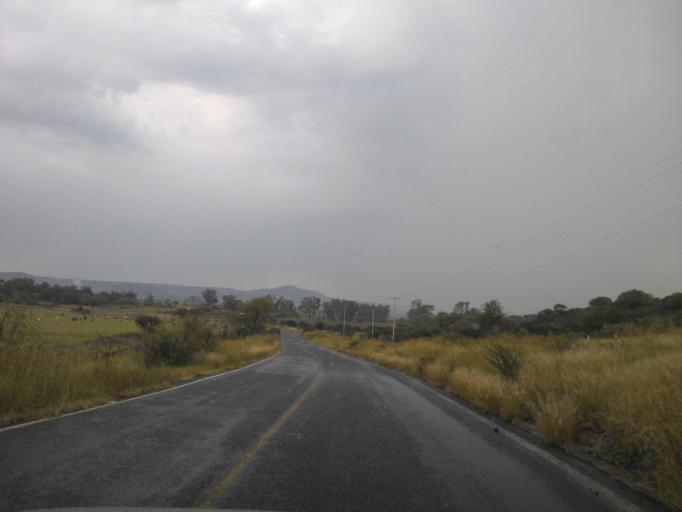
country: MX
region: Jalisco
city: San Diego de Alejandria
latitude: 20.8466
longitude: -102.1003
